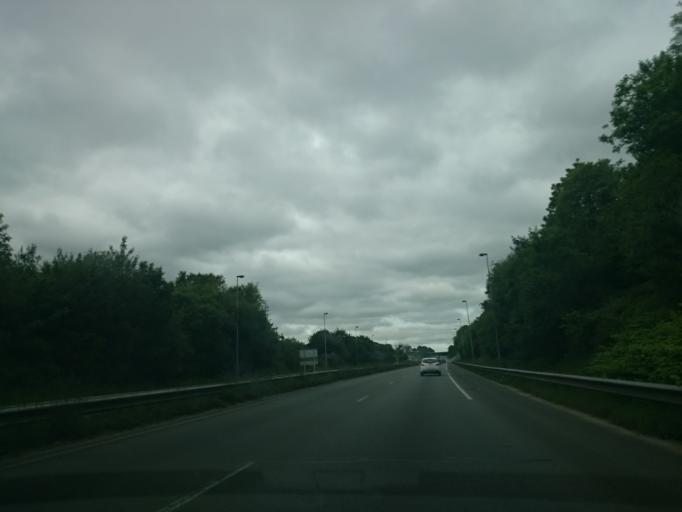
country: FR
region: Brittany
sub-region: Departement du Finistere
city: Brest
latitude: 48.4176
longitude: -4.4787
